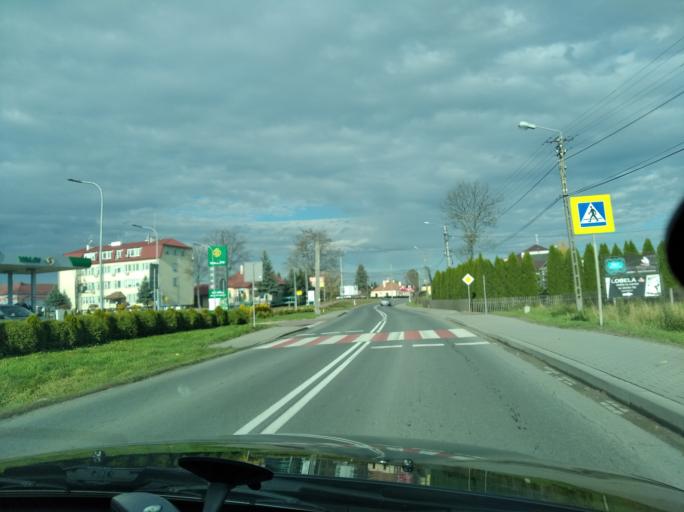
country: PL
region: Subcarpathian Voivodeship
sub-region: Powiat ropczycko-sedziszowski
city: Ostrow
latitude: 50.0976
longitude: 21.5936
